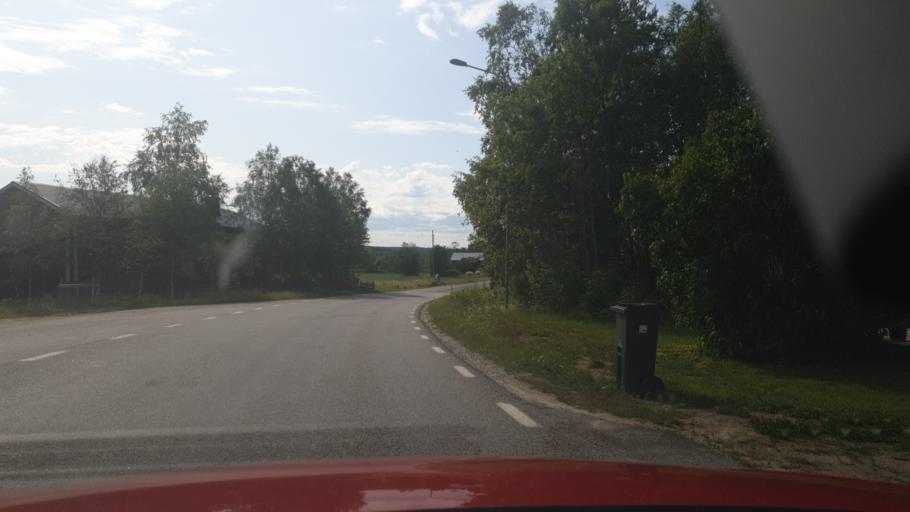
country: SE
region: Vaesternorrland
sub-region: Sundsvalls Kommun
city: Njurundabommen
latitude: 62.0414
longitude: 17.3092
